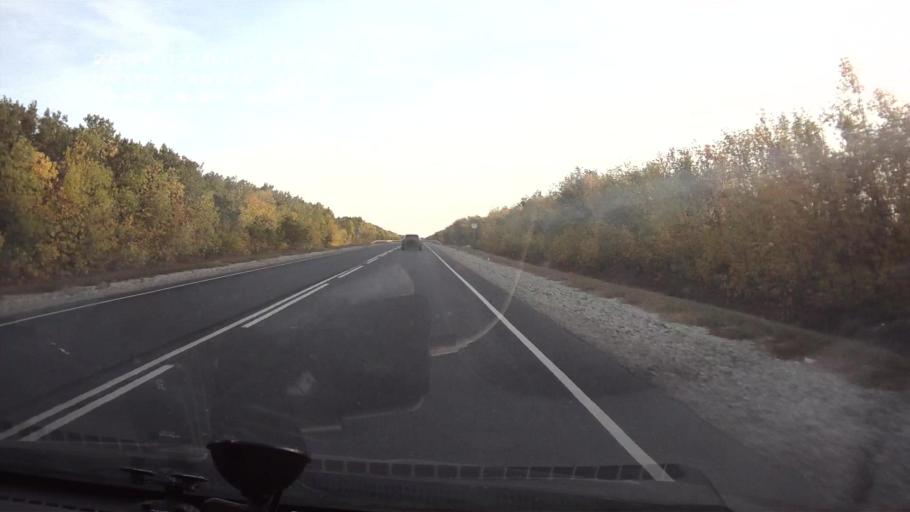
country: RU
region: Saratov
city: Krasnoarmeysk
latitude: 51.0937
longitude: 45.6476
